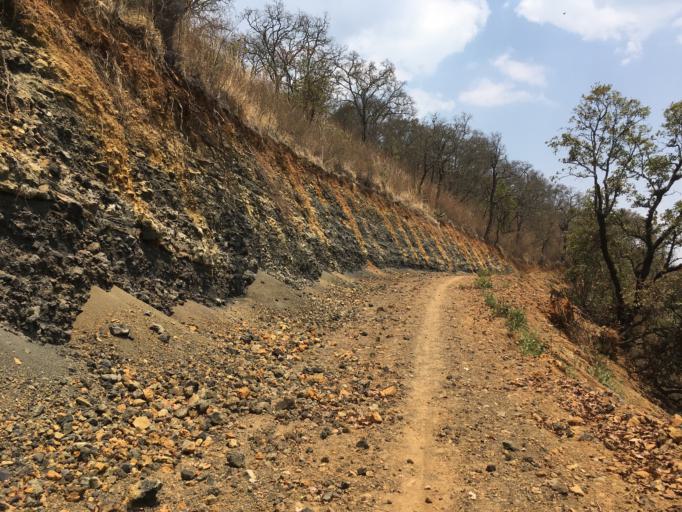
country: MX
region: Michoacan
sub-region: Patzcuaro
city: Santa Ana Chapitiro
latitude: 19.5114
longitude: -101.6444
